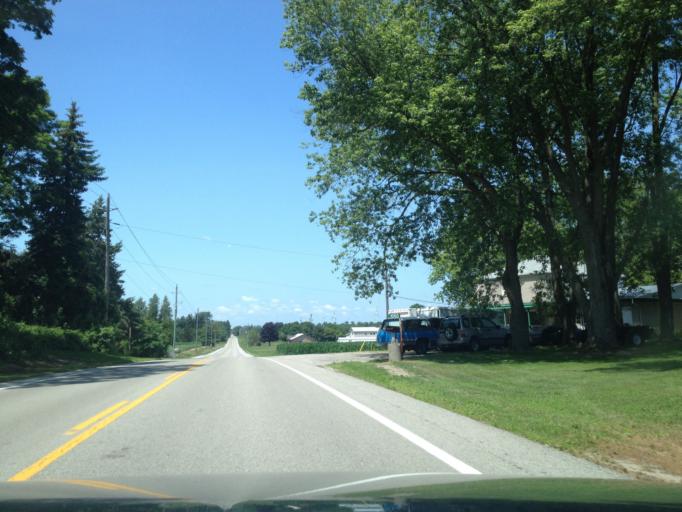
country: CA
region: Ontario
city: Norfolk County
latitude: 42.5903
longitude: -80.6313
